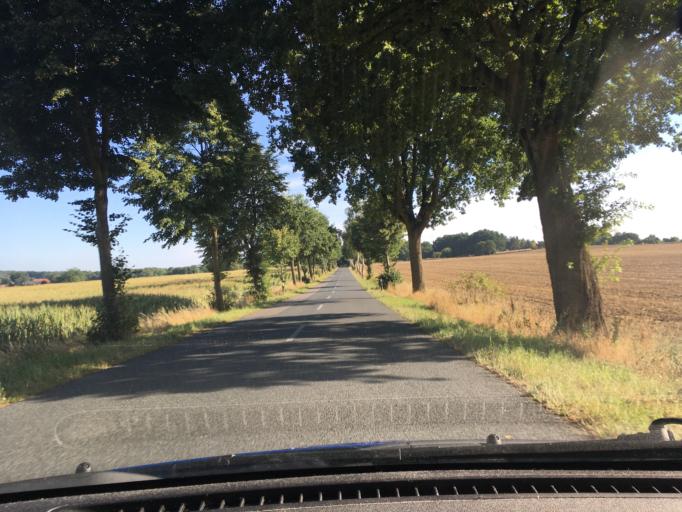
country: DE
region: Lower Saxony
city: Thomasburg
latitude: 53.2323
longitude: 10.7037
